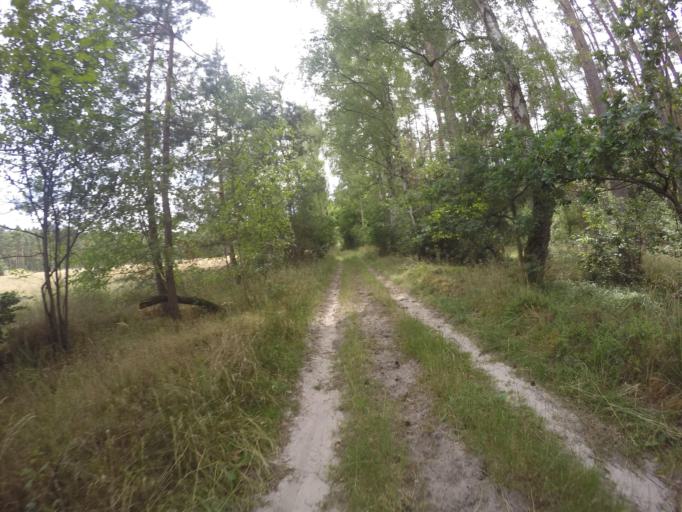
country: DE
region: Lower Saxony
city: Thomasburg
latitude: 53.2508
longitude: 10.6664
